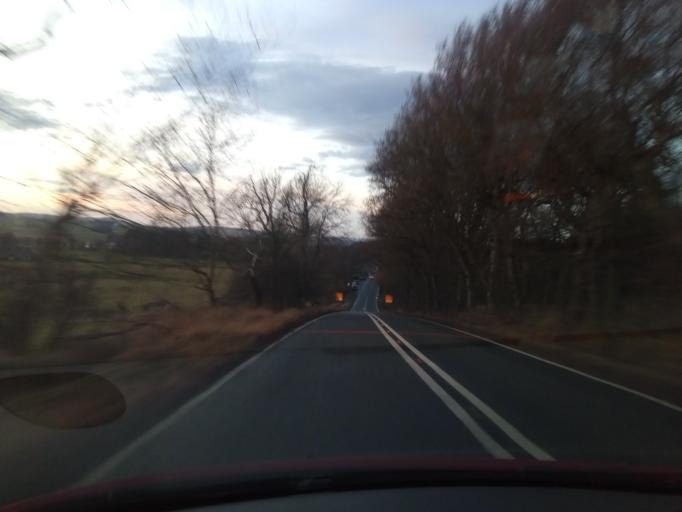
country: GB
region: England
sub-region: Northumberland
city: Otterburn
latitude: 55.2299
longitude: -2.1718
